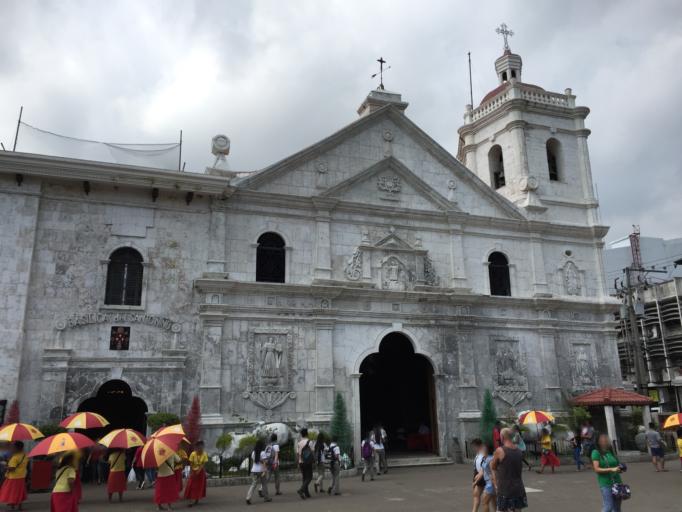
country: PH
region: Central Visayas
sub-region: Cebu City
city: Calero
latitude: 10.2942
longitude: 123.9024
